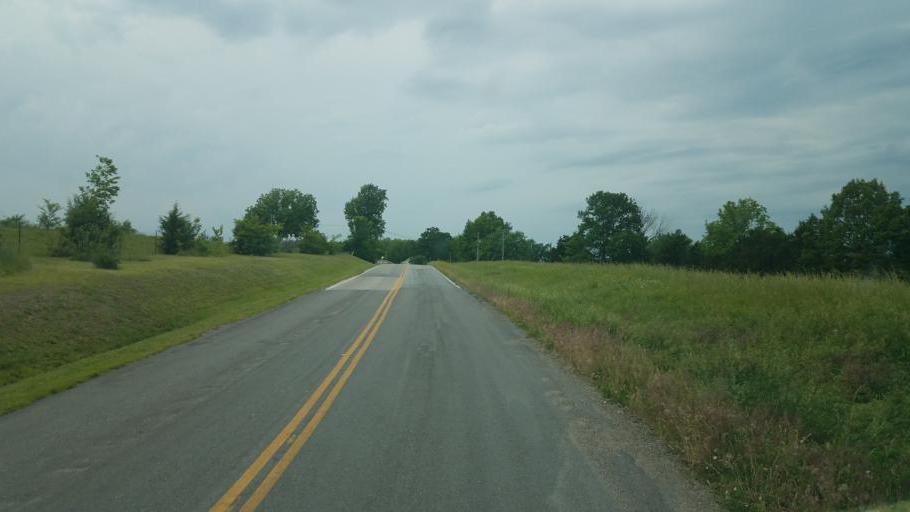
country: US
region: Missouri
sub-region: Moniteau County
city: California
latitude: 38.6563
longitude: -92.5749
